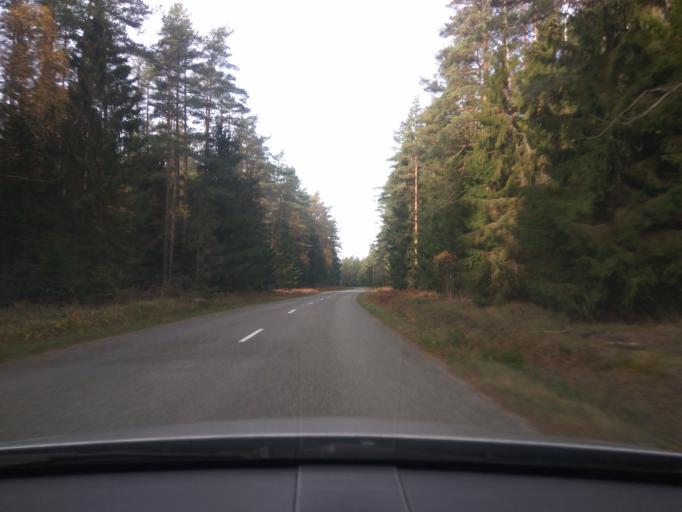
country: LV
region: Alsunga
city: Alsunga
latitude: 57.0119
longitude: 21.4395
